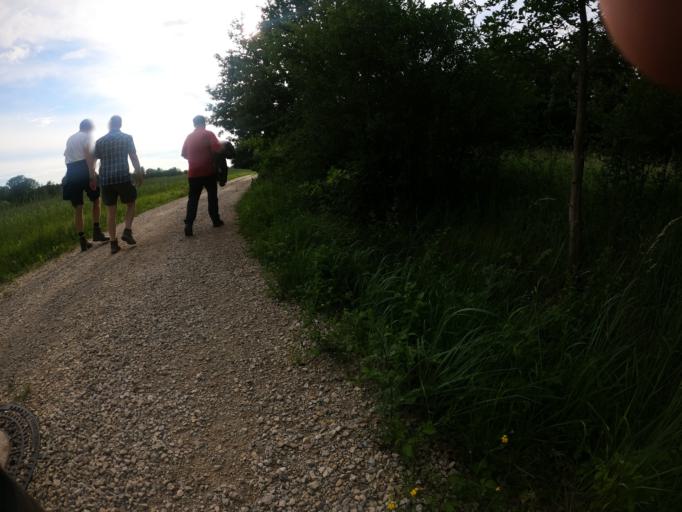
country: DE
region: Bavaria
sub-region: Upper Franconia
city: Memmelsdorf
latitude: 49.9256
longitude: 10.9662
